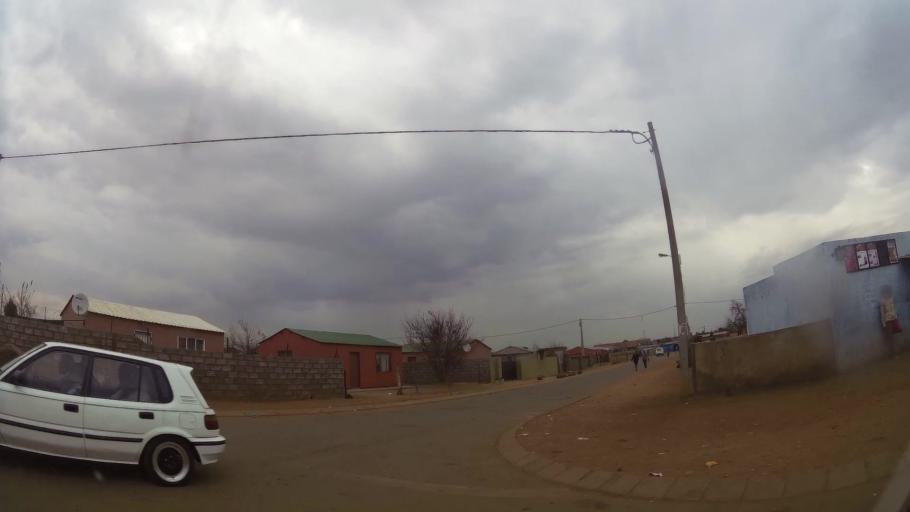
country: ZA
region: Gauteng
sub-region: Ekurhuleni Metropolitan Municipality
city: Germiston
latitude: -26.3860
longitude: 28.1383
